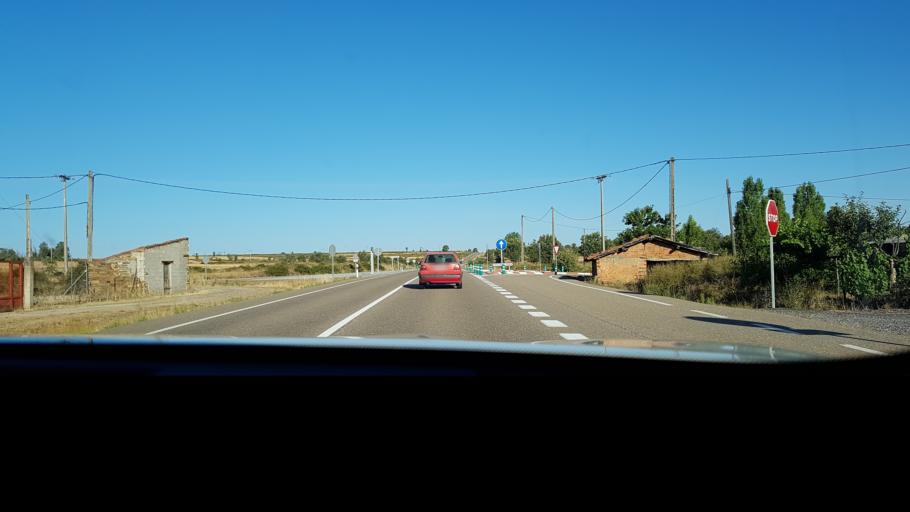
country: ES
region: Castille and Leon
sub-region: Provincia de Zamora
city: Rabanales
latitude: 41.6846
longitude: -6.2798
